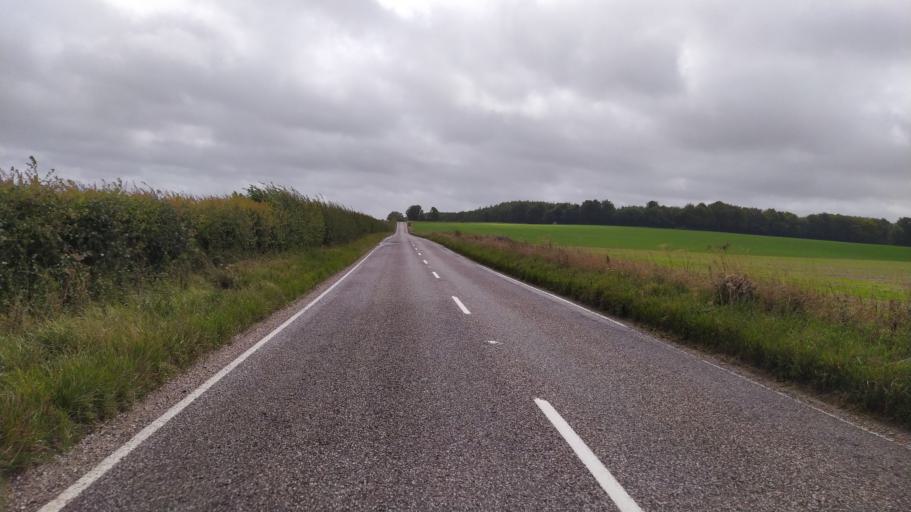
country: GB
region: England
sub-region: Wiltshire
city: Bower Chalke
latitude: 50.9322
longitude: -1.9578
